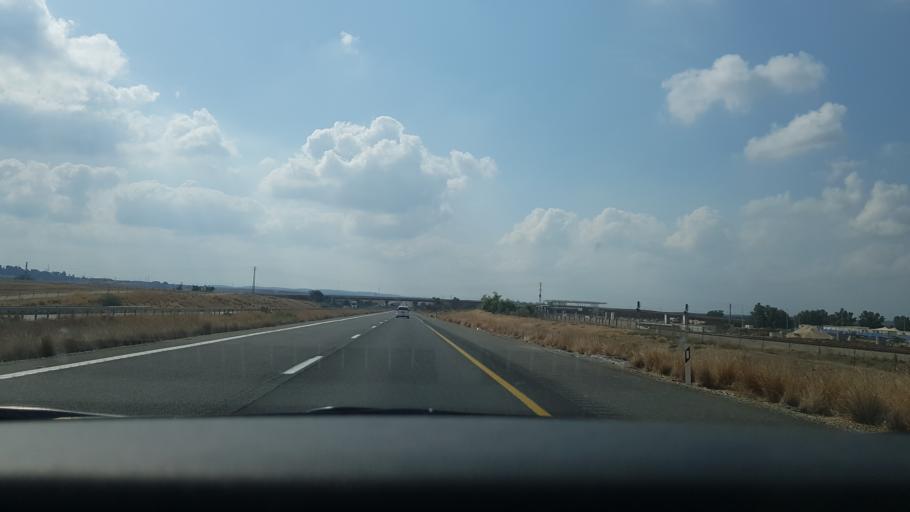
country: IL
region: Central District
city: Gedera
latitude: 31.7500
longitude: 34.8234
